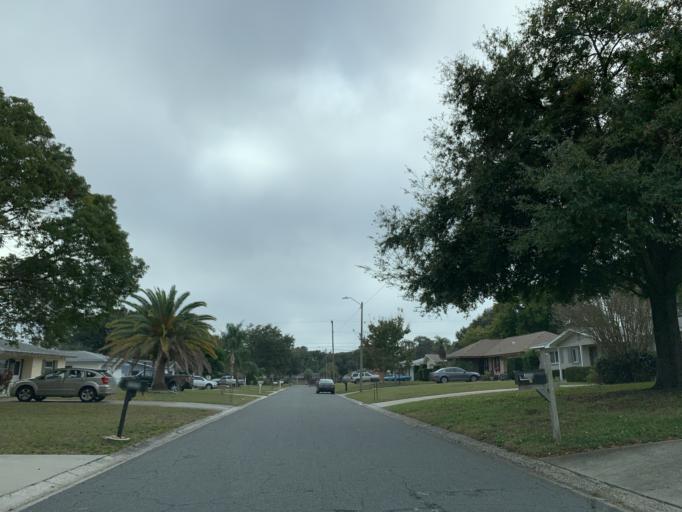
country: US
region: Florida
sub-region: Pinellas County
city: South Highpoint
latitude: 27.9518
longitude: -82.7347
